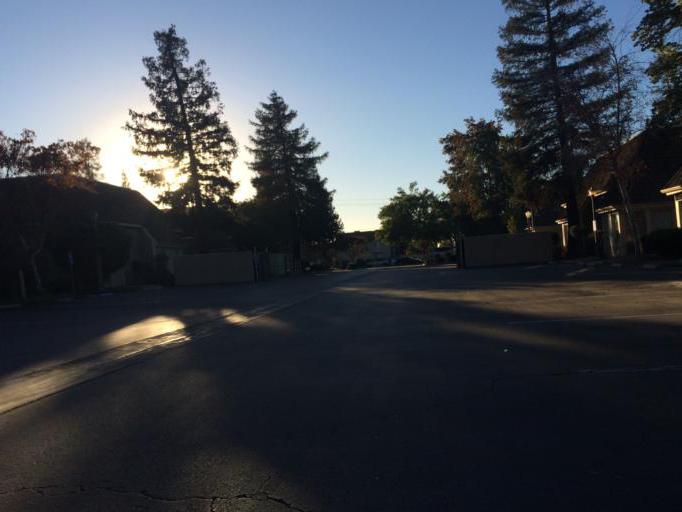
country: US
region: California
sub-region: Fresno County
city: Sunnyside
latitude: 36.7695
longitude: -119.7306
